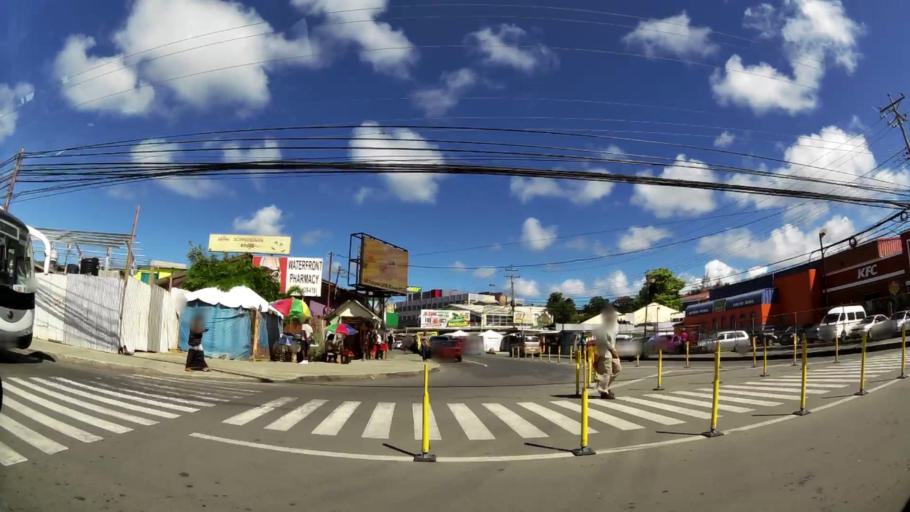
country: TT
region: Tobago
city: Scarborough
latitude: 11.1828
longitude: -60.7374
